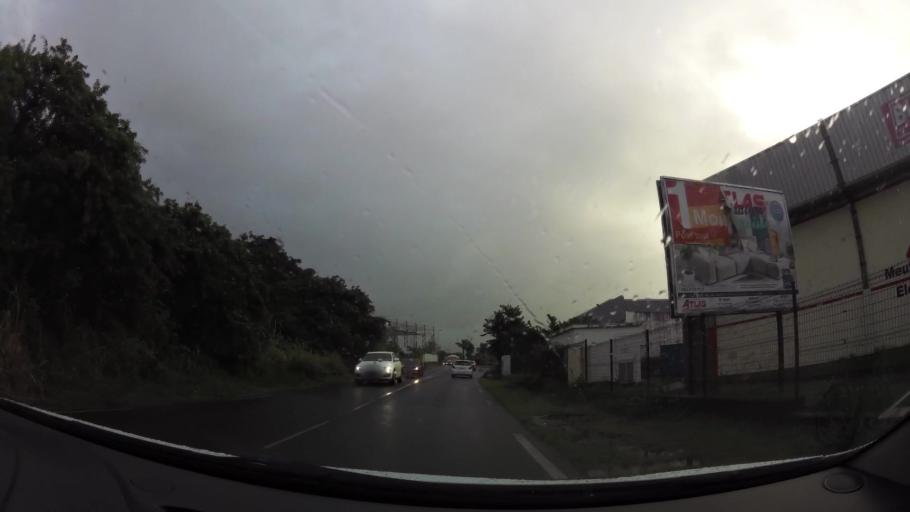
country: RE
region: Reunion
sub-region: Reunion
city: Saint-Andre
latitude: -20.9622
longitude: 55.6602
